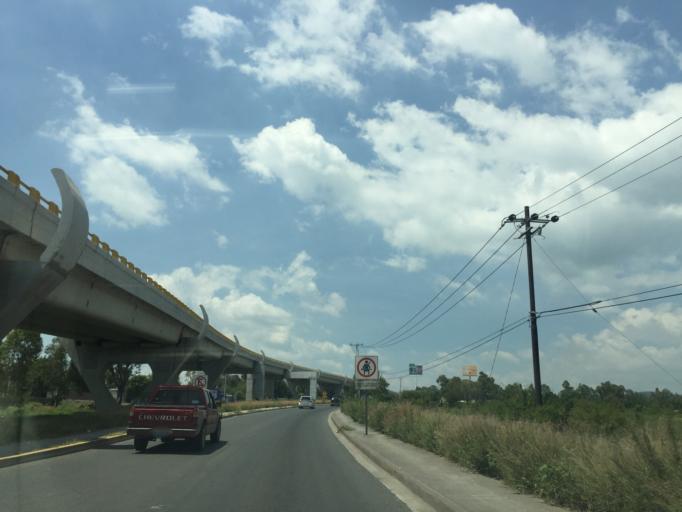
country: MX
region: Guanajuato
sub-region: Leon
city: Fraccionamiento Paseo de las Torres
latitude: 21.1772
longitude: -101.7402
